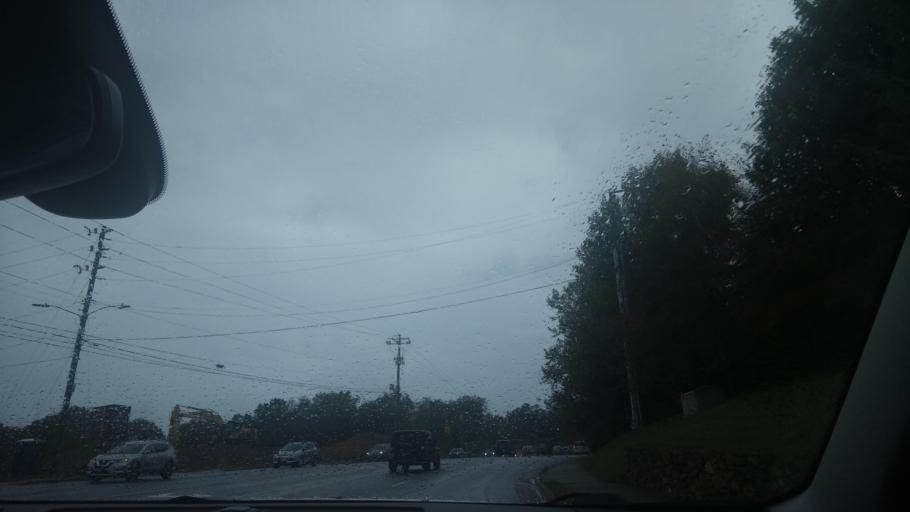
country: US
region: North Carolina
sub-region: Buncombe County
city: Biltmore Forest
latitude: 35.5565
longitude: -82.5382
